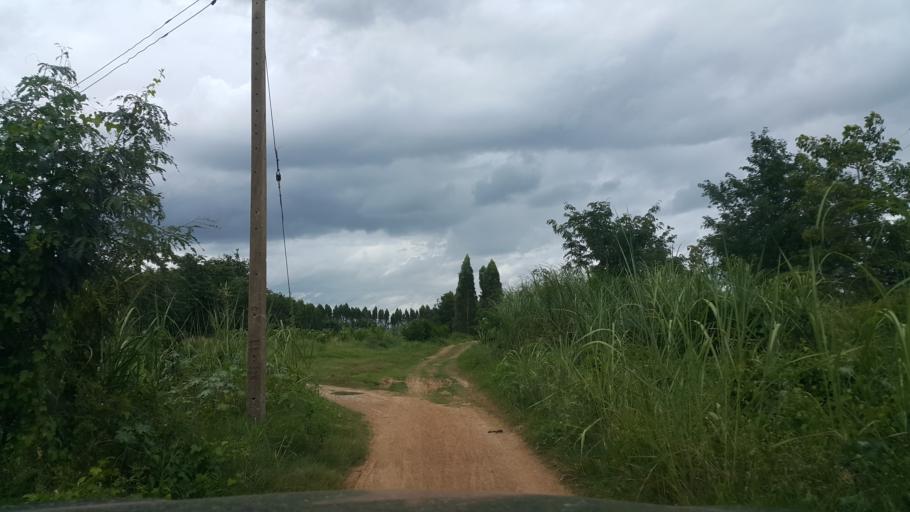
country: TH
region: Sukhothai
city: Sukhothai
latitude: 17.0265
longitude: 99.7982
